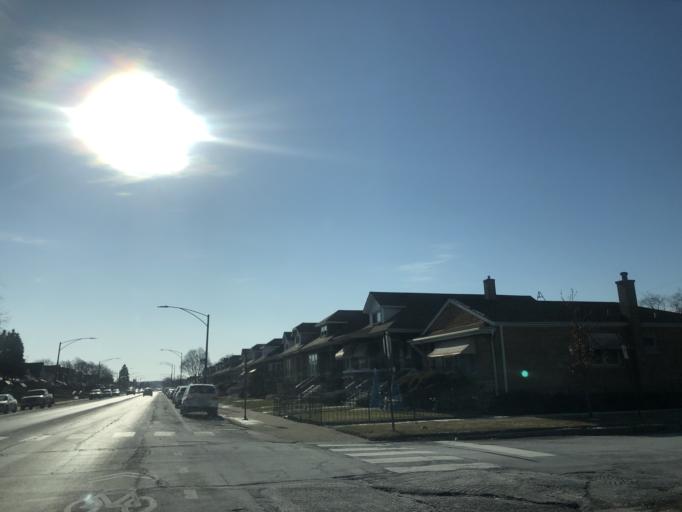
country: US
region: Illinois
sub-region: Cook County
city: Evergreen Park
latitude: 41.7541
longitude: -87.6732
